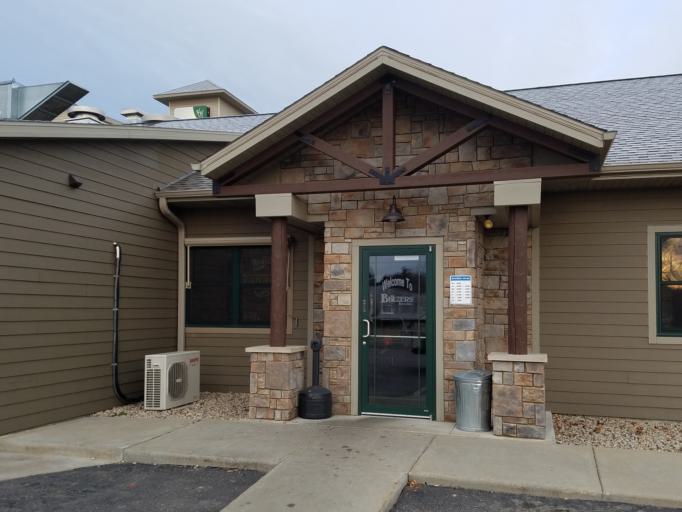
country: US
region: Wisconsin
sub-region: Vernon County
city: Hillsboro
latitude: 43.6555
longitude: -90.3357
